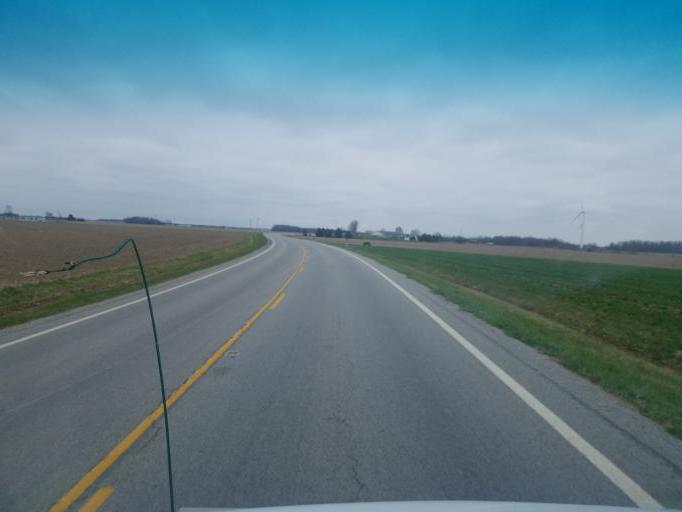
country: US
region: Ohio
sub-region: Van Wert County
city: Van Wert
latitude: 40.9210
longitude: -84.5457
